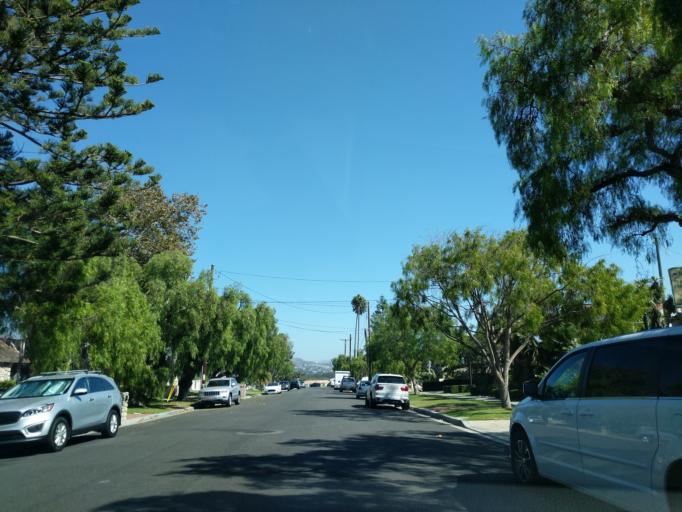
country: US
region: California
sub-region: Orange County
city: Dana Point
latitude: 33.4635
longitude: -117.7002
